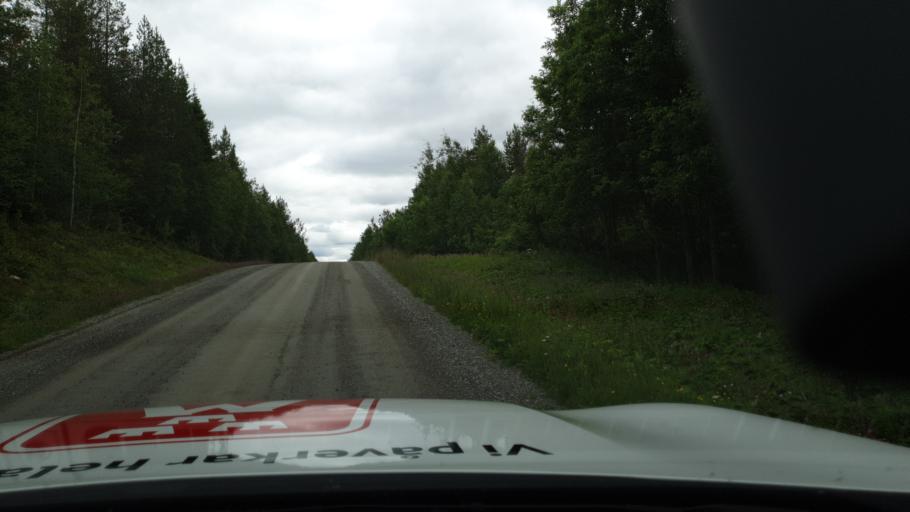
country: SE
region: Vaesterbotten
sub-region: Storumans Kommun
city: Storuman
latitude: 64.7780
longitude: 17.0362
